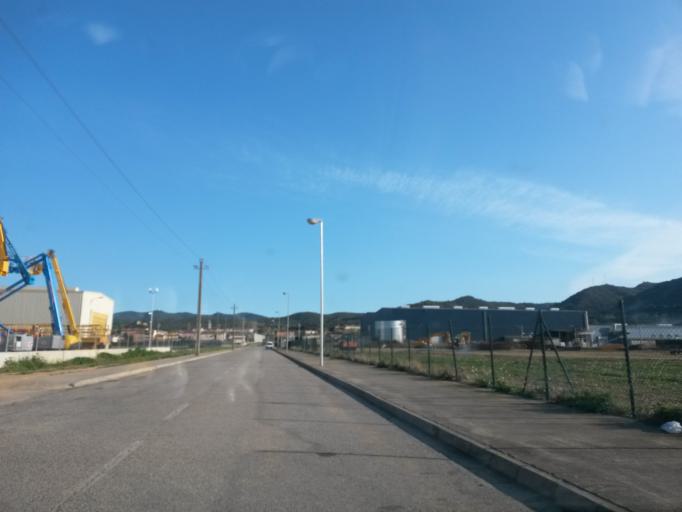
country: ES
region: Catalonia
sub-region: Provincia de Girona
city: Celra
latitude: 42.0331
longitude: 2.8744
